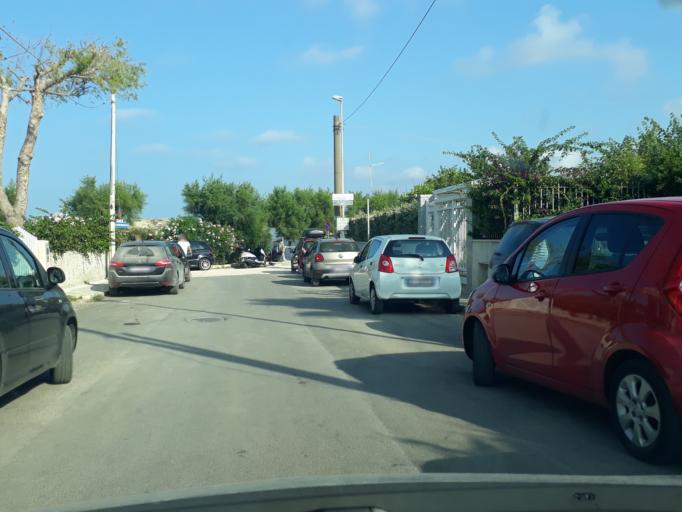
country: IT
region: Apulia
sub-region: Provincia di Brindisi
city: Carovigno
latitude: 40.7594
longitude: 17.6965
